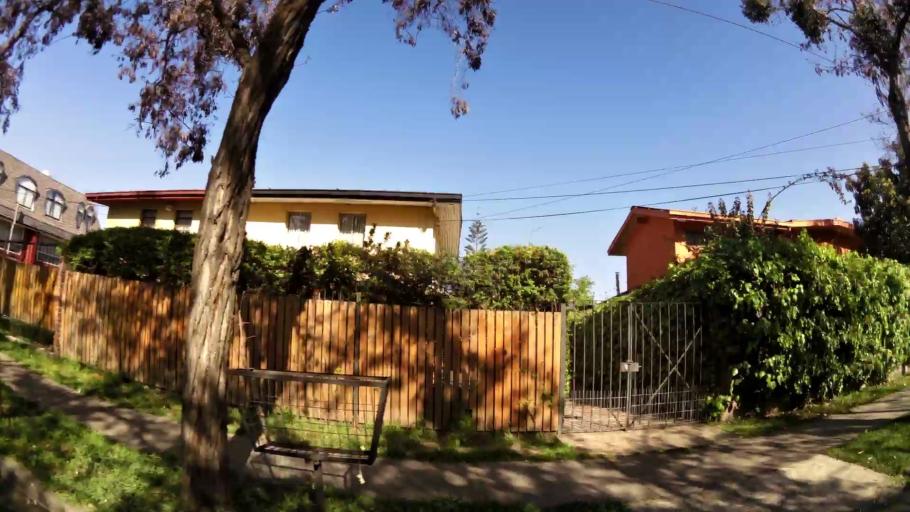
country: CL
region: Santiago Metropolitan
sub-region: Provincia de Santiago
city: Villa Presidente Frei, Nunoa, Santiago, Chile
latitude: -33.4406
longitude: -70.5753
